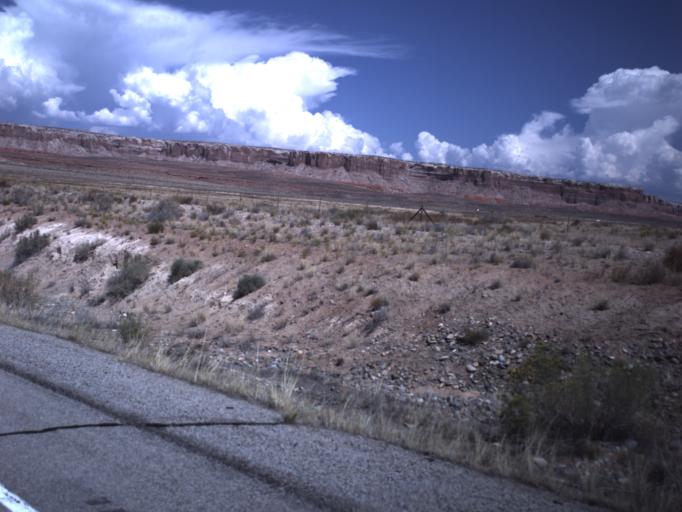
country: US
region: Utah
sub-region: San Juan County
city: Blanding
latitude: 37.2539
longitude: -109.6146
